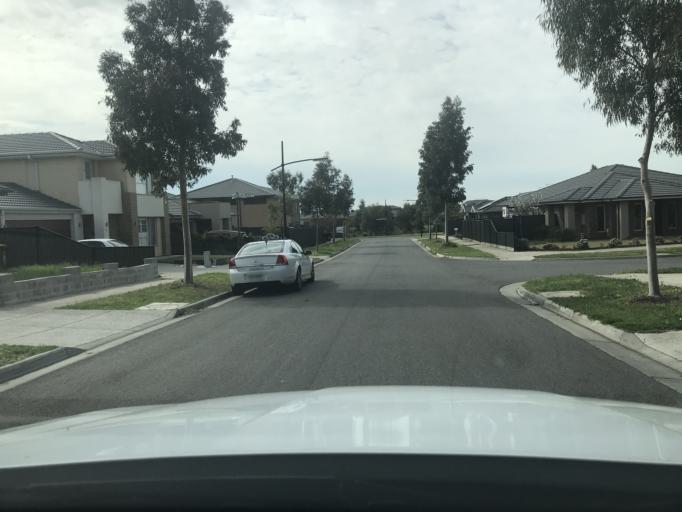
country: AU
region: Victoria
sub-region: Hume
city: Roxburgh Park
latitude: -37.5966
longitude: 144.8961
